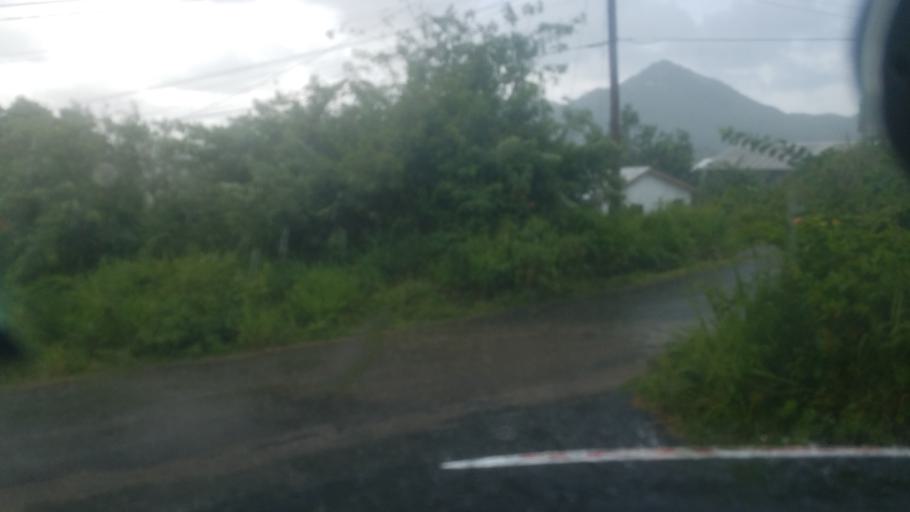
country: LC
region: Laborie Quarter
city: Laborie
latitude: 13.7457
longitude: -60.9670
